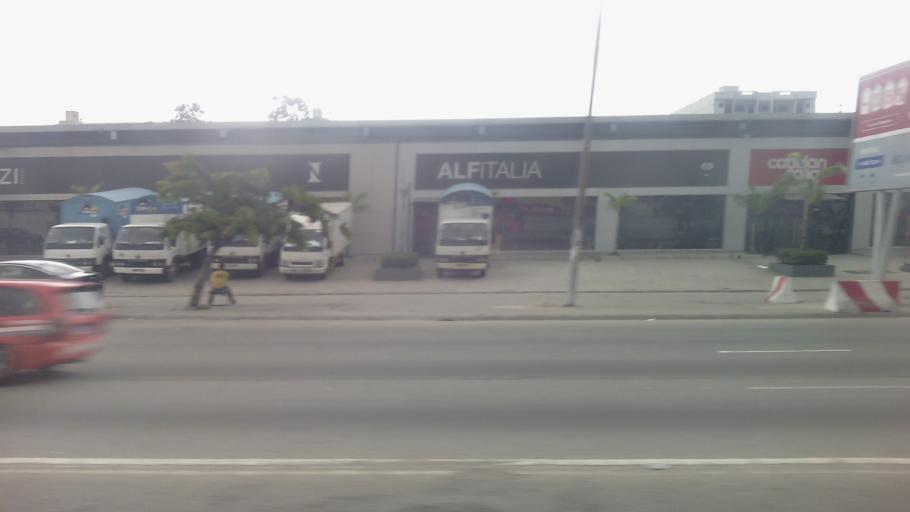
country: CI
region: Lagunes
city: Abidjan
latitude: 5.2913
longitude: -3.9728
